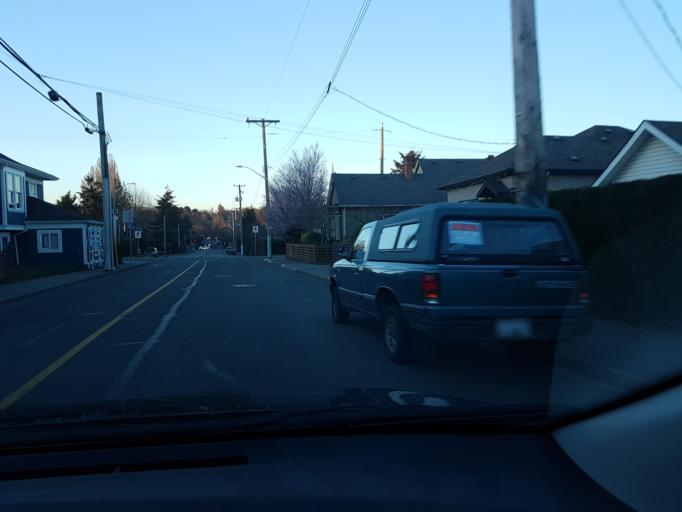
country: CA
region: British Columbia
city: Victoria
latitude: 48.4323
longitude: -123.3451
